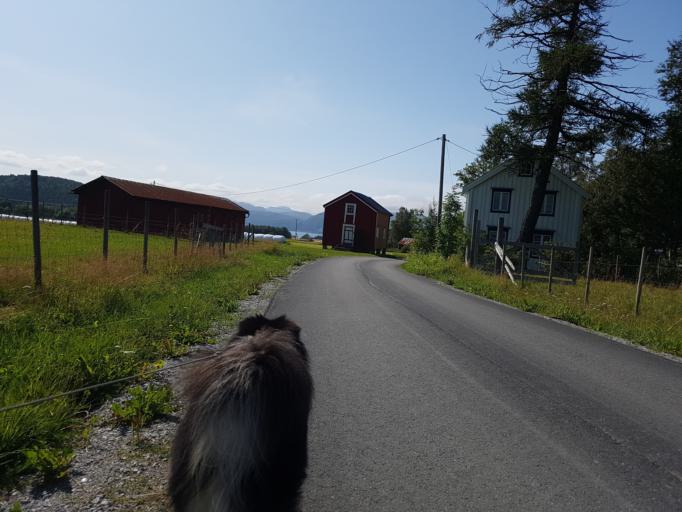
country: NO
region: Sor-Trondelag
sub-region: Agdenes
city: Lensvik
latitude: 63.6303
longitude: 9.8363
